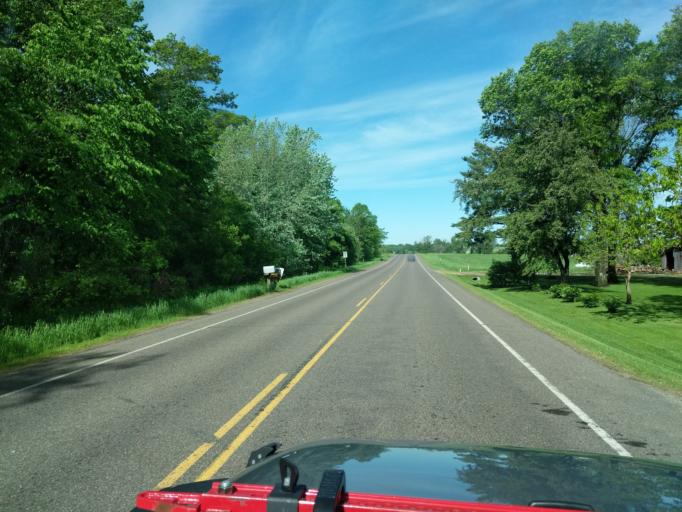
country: US
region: Wisconsin
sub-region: Pierce County
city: River Falls
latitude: 44.8697
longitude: -92.4993
